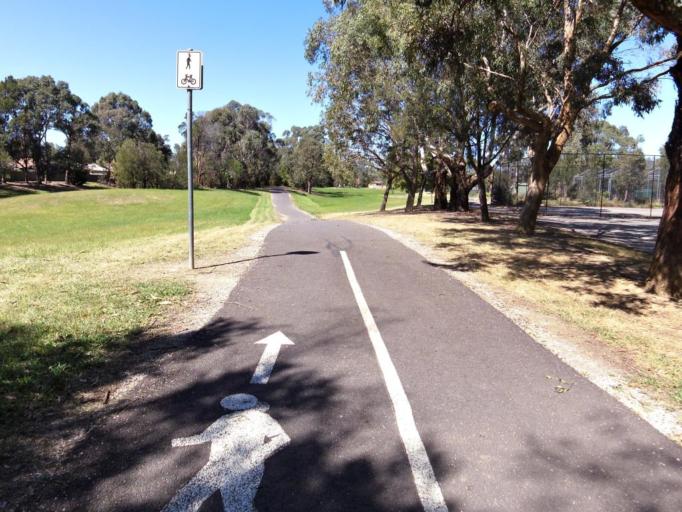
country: AU
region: Victoria
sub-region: Knox
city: Rowville
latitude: -37.9310
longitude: 145.2418
